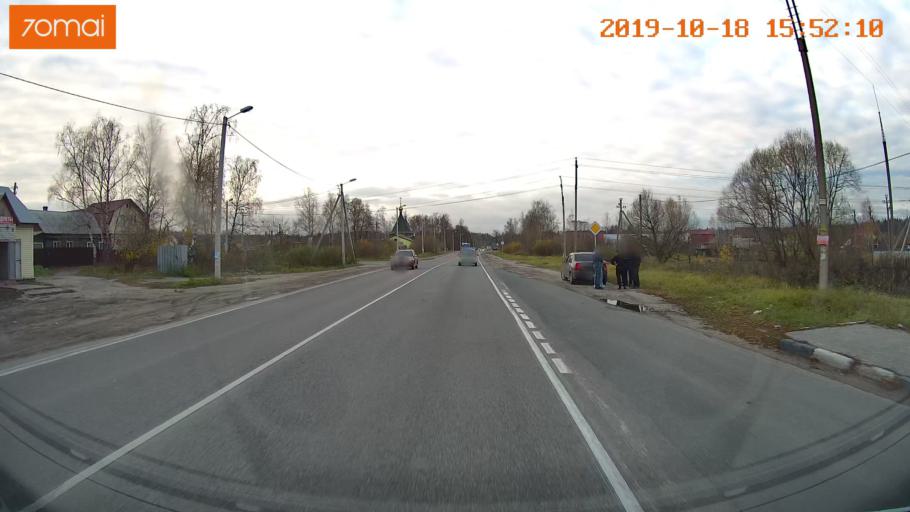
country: RU
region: Vladimir
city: Kommunar
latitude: 56.0459
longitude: 40.5385
